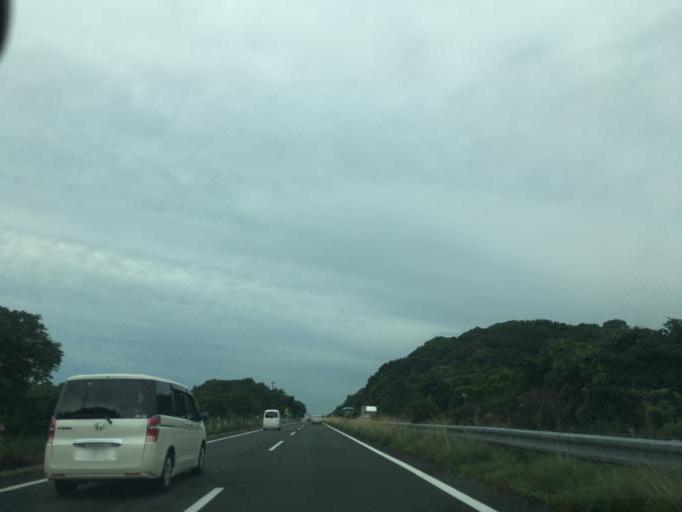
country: JP
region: Saga Prefecture
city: Kanzakimachi-kanzaki
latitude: 33.3605
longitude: 130.4351
